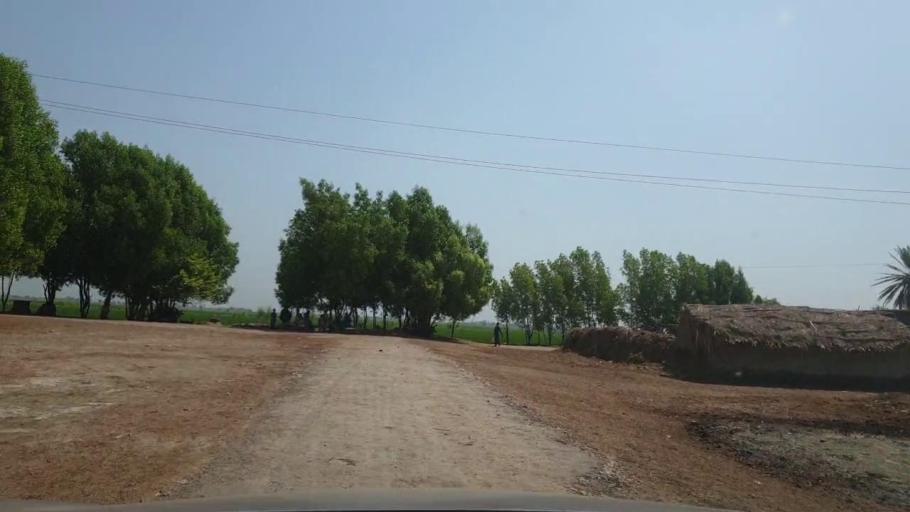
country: PK
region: Sindh
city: Warah
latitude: 27.4841
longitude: 67.7801
